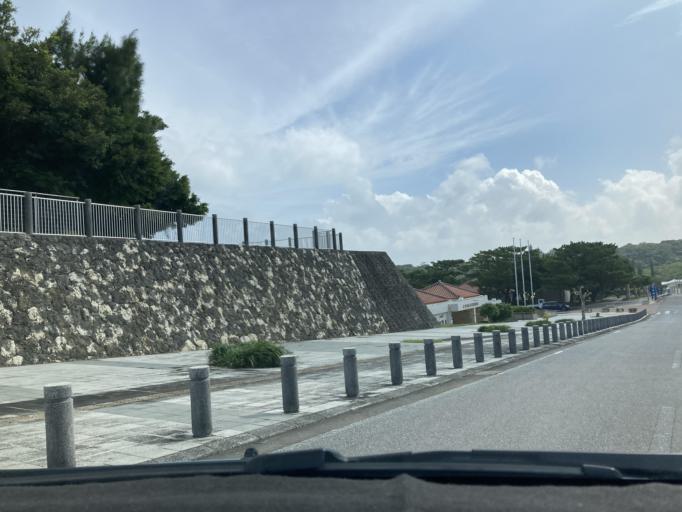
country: JP
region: Okinawa
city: Itoman
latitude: 26.0978
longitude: 127.7231
